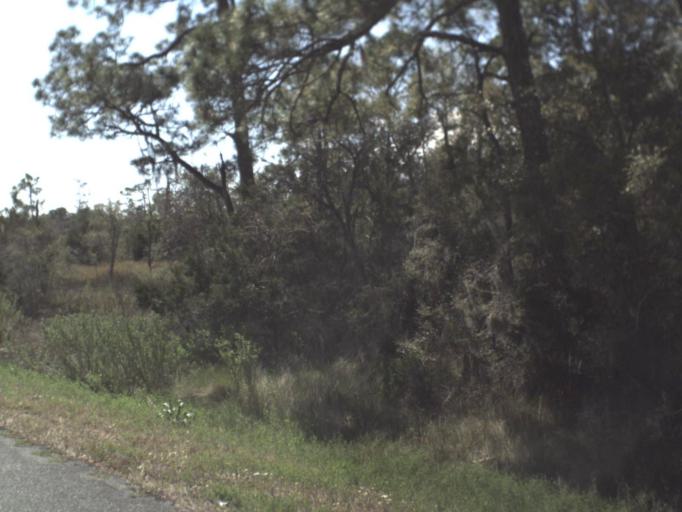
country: US
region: Florida
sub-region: Wakulla County
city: Crawfordville
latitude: 30.0165
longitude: -84.3926
